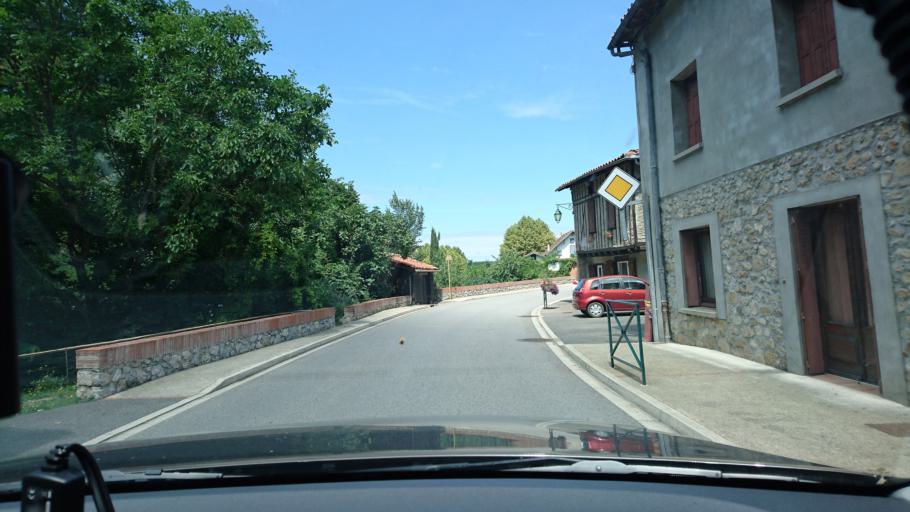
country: FR
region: Midi-Pyrenees
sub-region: Departement de la Haute-Garonne
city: Gaillac-Toulza
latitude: 43.1009
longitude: 1.4427
